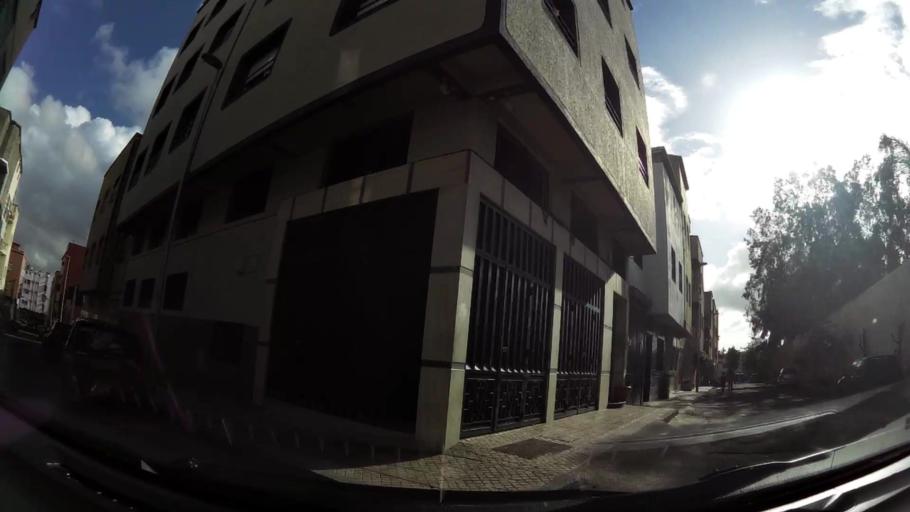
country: MA
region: Grand Casablanca
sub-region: Casablanca
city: Casablanca
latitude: 33.5422
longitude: -7.5972
